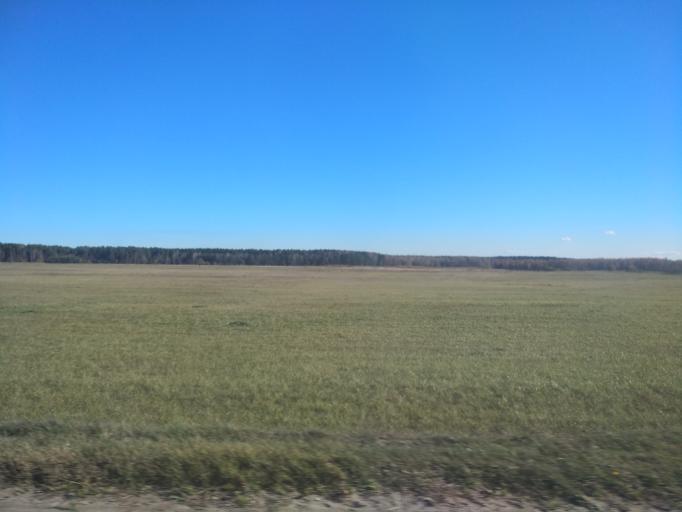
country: BY
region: Minsk
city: Il'ya
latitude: 54.5558
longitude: 27.2134
